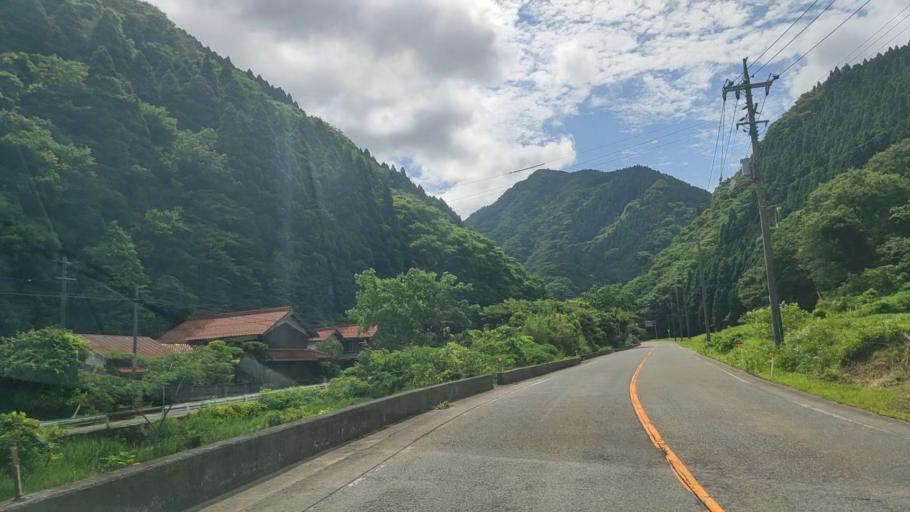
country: JP
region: Okayama
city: Niimi
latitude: 35.2131
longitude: 133.4648
